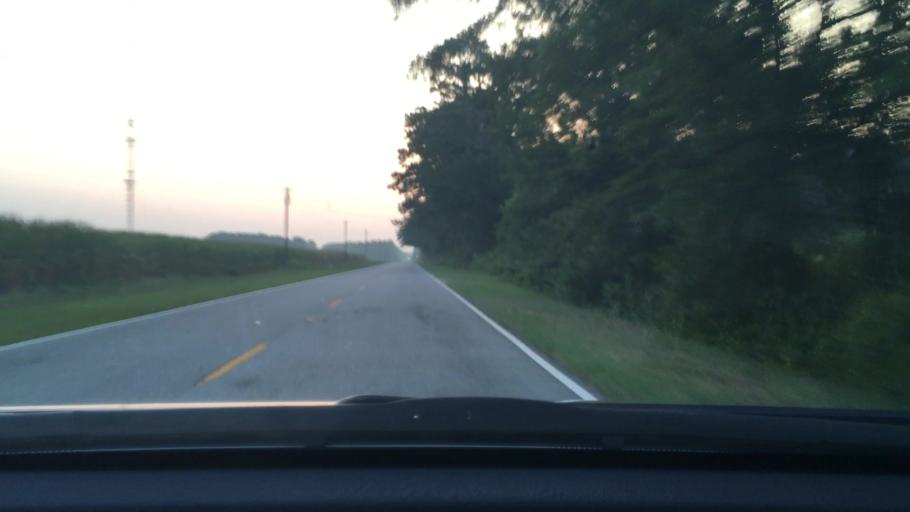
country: US
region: South Carolina
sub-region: Lee County
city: Bishopville
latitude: 34.1144
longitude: -80.1506
